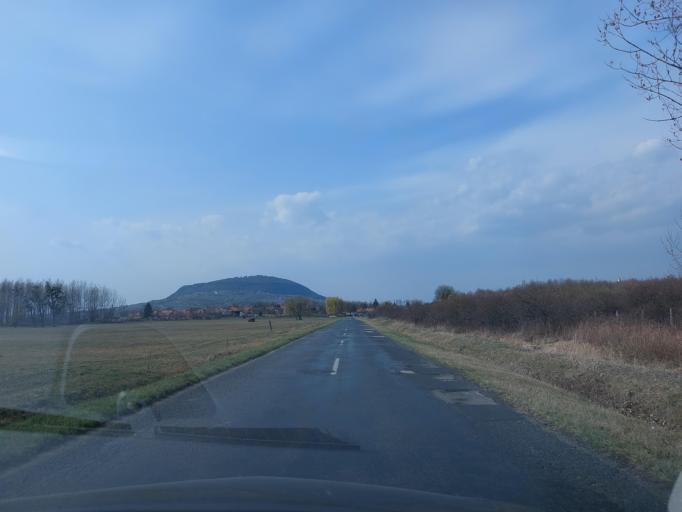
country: HU
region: Veszprem
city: Devecser
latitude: 47.1272
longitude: 17.4053
